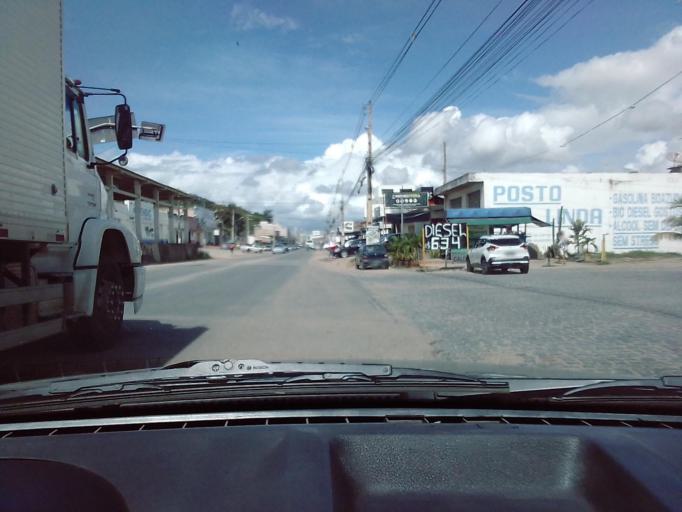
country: BR
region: Pernambuco
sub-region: Vitoria De Santo Antao
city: Vitoria de Santo Antao
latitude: -8.1177
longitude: -35.3039
